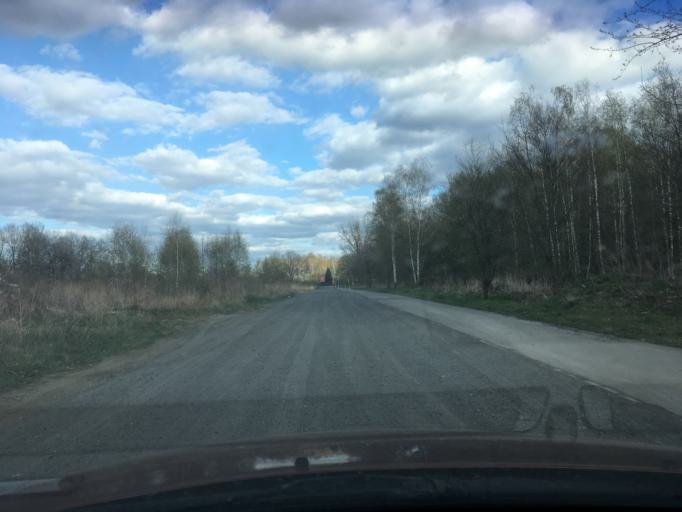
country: PL
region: Lower Silesian Voivodeship
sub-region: Powiat zgorzelecki
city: Zgorzelec
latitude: 51.1243
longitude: 15.0133
